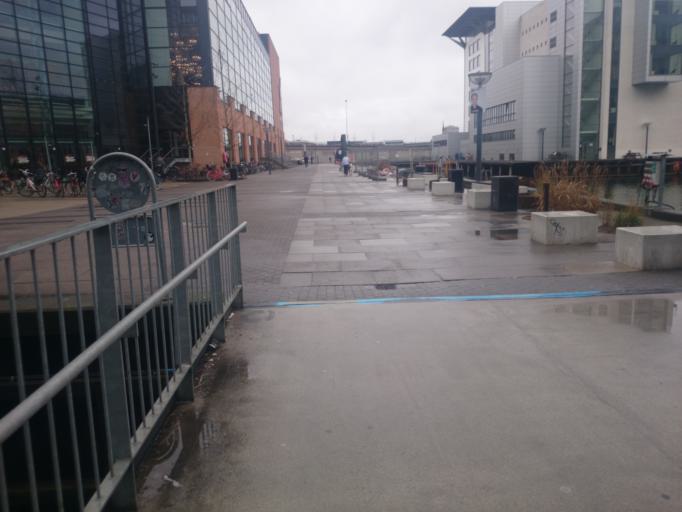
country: DK
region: Capital Region
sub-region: Kobenhavn
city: Copenhagen
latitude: 55.6624
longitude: 12.5638
